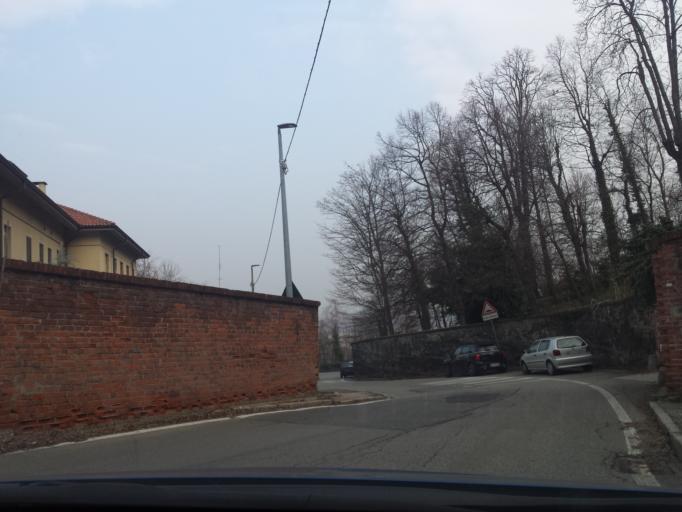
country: IT
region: Piedmont
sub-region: Provincia di Torino
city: Turin
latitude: 45.0567
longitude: 7.7067
